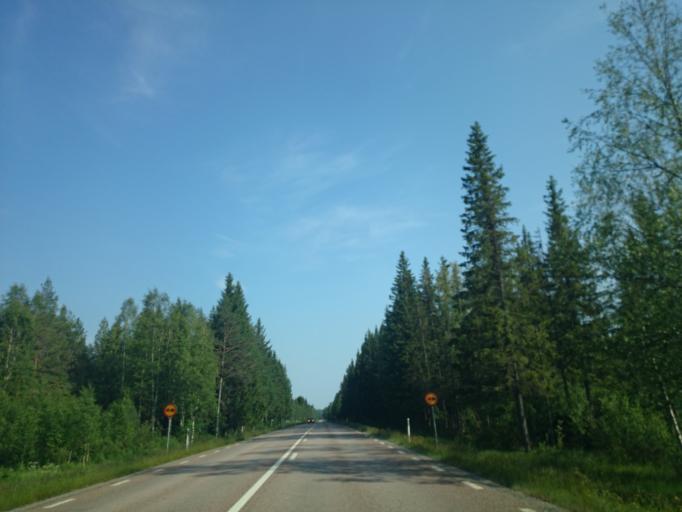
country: SE
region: Jaemtland
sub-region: OEstersunds Kommun
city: Brunflo
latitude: 62.9862
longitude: 14.9903
